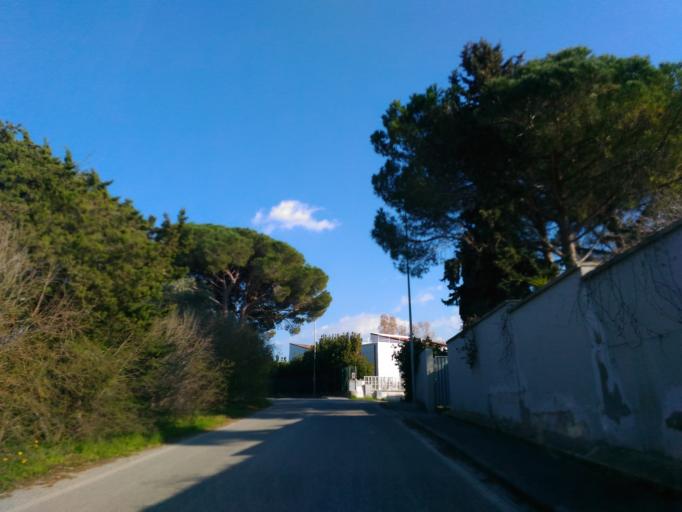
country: IT
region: Tuscany
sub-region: Provincia di Livorno
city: Livorno
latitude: 43.5100
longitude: 10.3401
